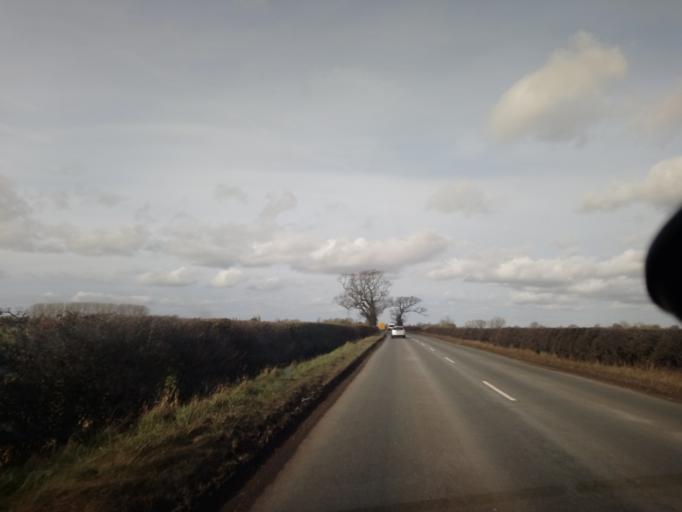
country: GB
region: England
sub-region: Telford and Wrekin
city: Eyton upon the Weald Moors
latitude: 52.7488
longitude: -2.5425
